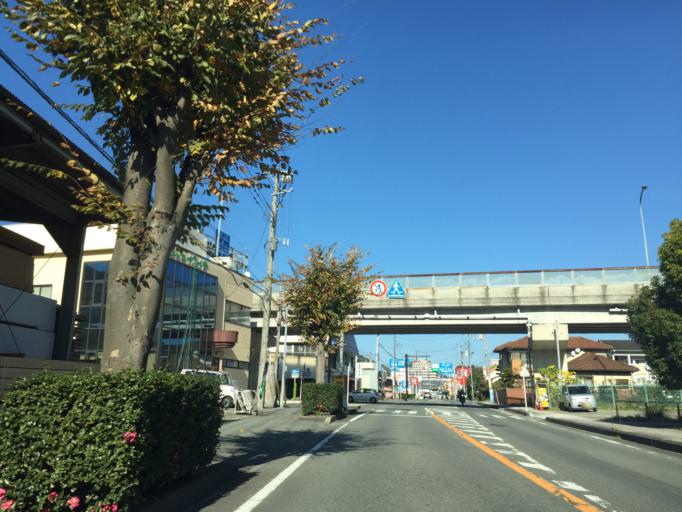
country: JP
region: Shizuoka
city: Mishima
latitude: 35.0253
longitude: 138.9298
